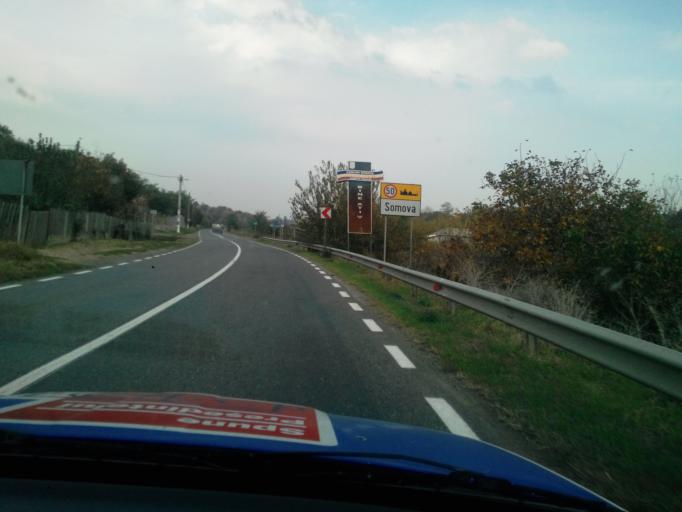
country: RO
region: Tulcea
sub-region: Comuna Somova
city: Somova
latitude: 45.1876
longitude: 28.6475
